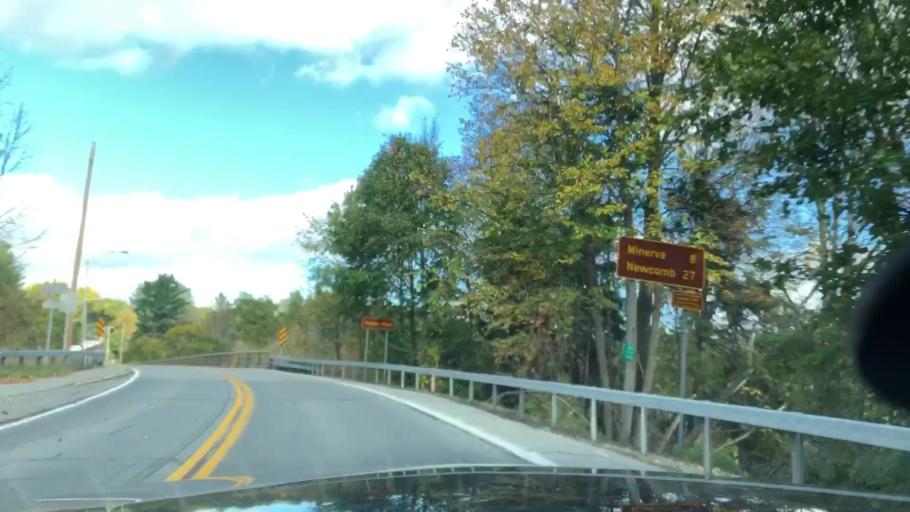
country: US
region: New York
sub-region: Warren County
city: Warrensburg
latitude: 43.6992
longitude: -73.9833
